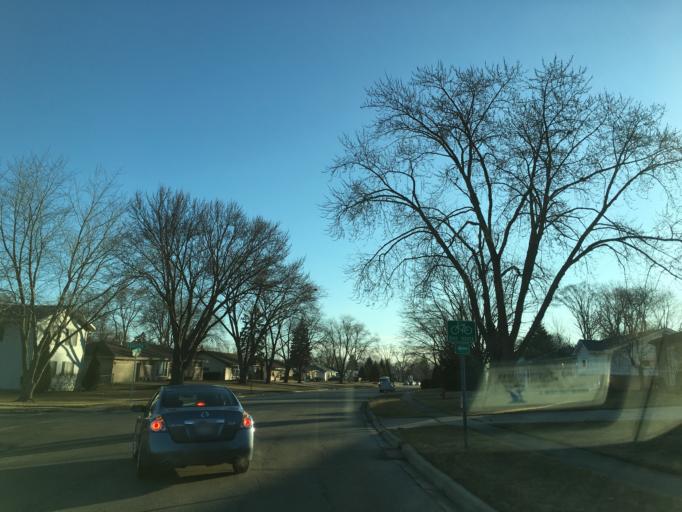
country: US
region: Illinois
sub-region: Cook County
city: Hoffman Estates
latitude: 42.0392
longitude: -88.0835
